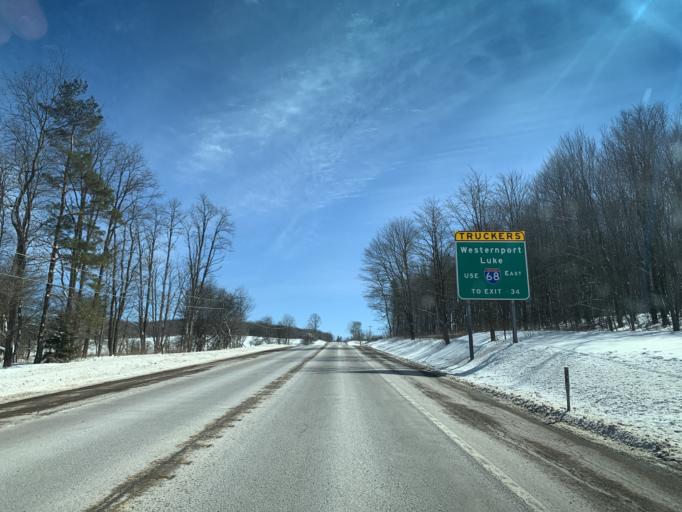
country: US
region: Pennsylvania
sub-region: Somerset County
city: Meyersdale
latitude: 39.7155
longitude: -79.2844
